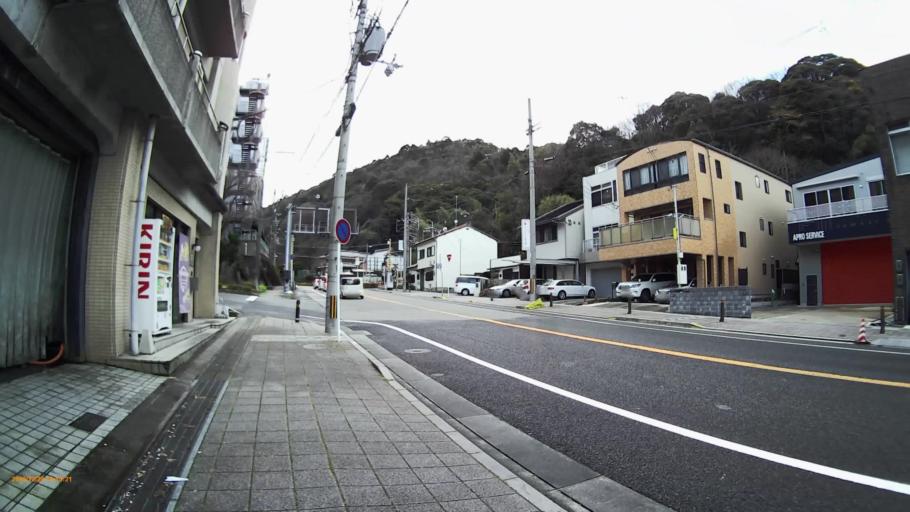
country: JP
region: Shiga Prefecture
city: Otsu-shi
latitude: 35.0019
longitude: 135.8593
